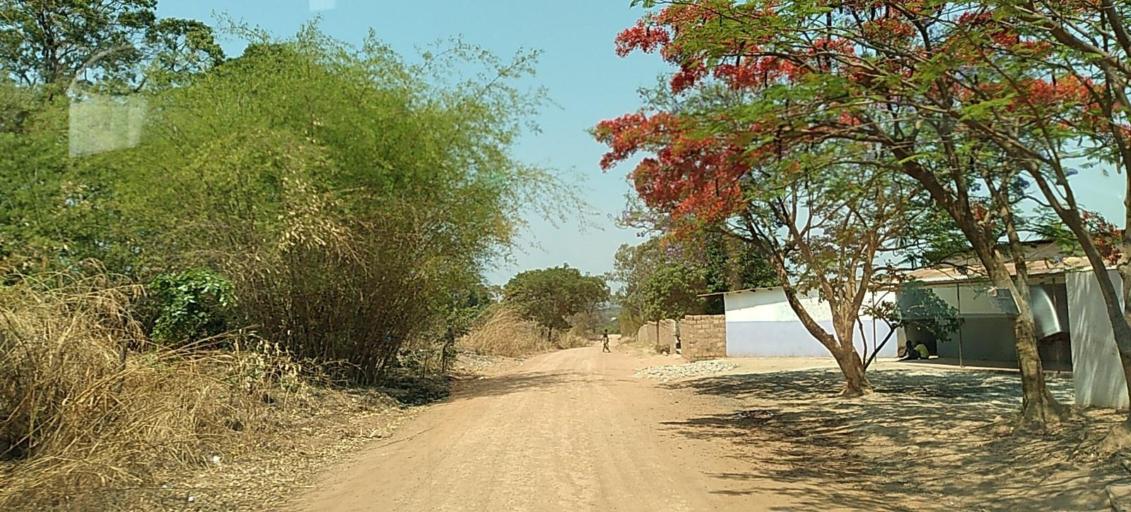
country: ZM
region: Copperbelt
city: Chambishi
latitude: -12.6050
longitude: 27.9627
